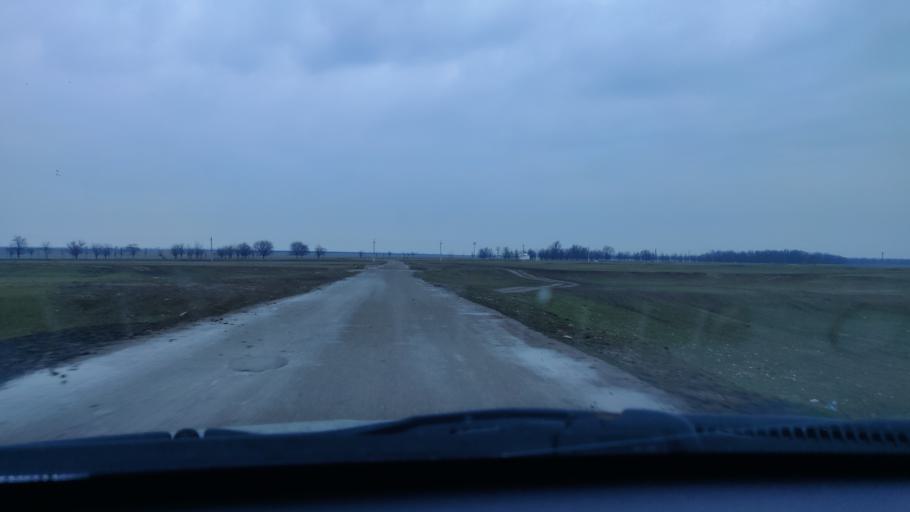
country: RU
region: Stavropol'skiy
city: Letnyaya Stavka
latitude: 45.4133
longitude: 43.7040
